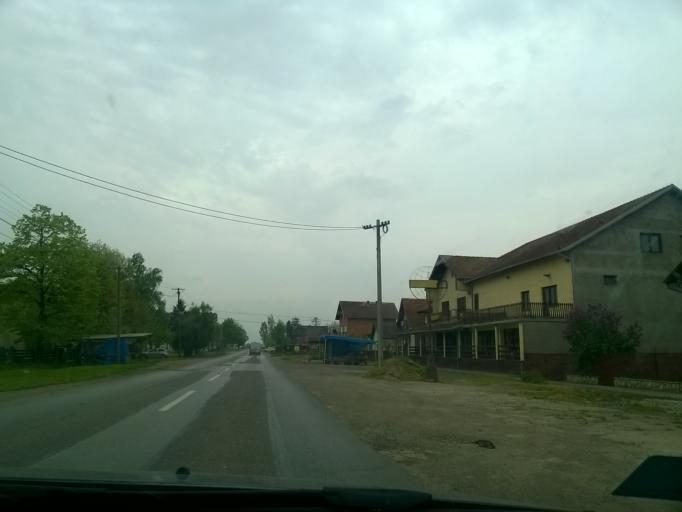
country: RS
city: Hrtkovci
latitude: 44.8709
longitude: 19.7701
